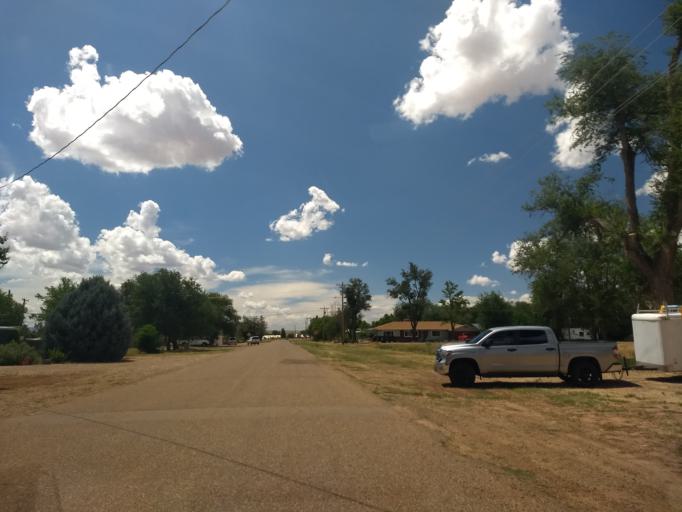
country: US
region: Arizona
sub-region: Coconino County
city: Fredonia
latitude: 36.9481
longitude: -112.5243
